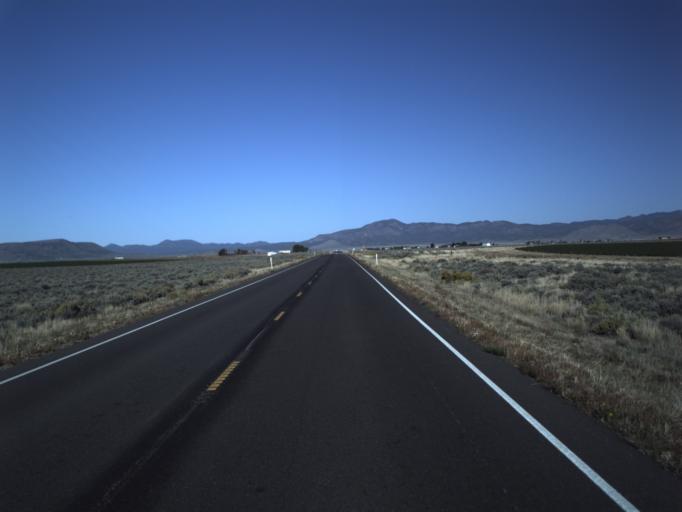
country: US
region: Utah
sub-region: Washington County
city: Enterprise
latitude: 37.7505
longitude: -113.7710
